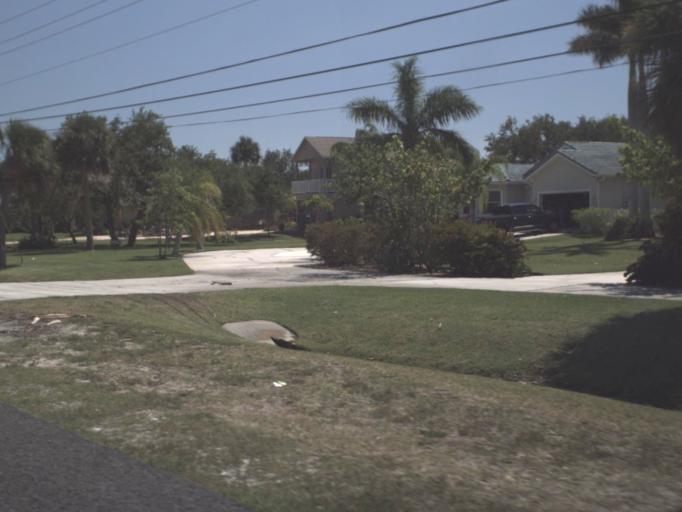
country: US
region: Florida
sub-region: Brevard County
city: Grant-Valkaria
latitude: 27.9424
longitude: -80.5323
